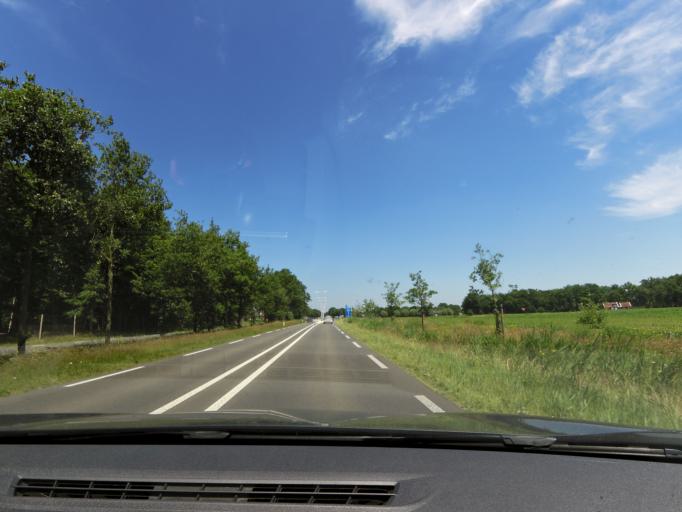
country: NL
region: Overijssel
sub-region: Gemeente Wierden
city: Wierden
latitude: 52.3311
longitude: 6.5528
